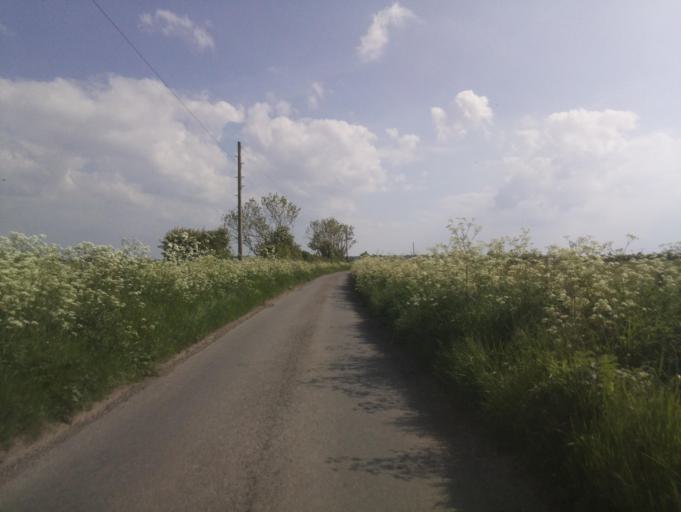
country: GB
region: England
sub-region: South Gloucestershire
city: Horton
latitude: 51.5776
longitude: -2.3188
